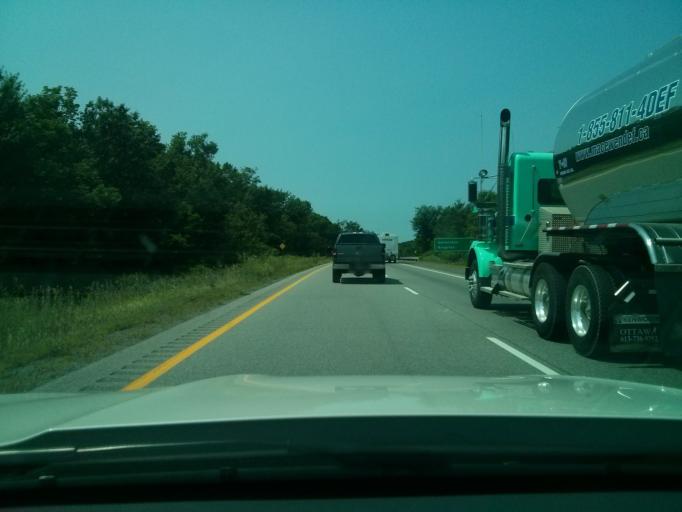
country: CA
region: Ontario
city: Brockville
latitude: 44.5202
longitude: -75.7858
